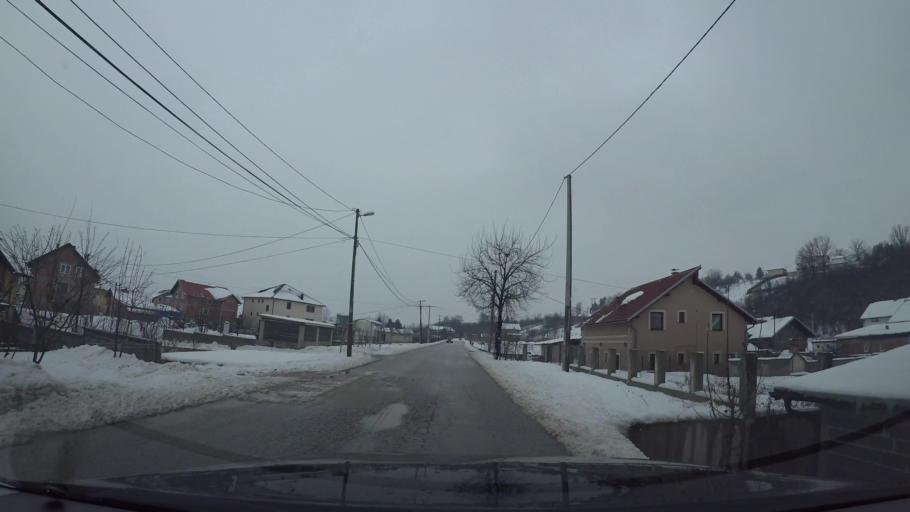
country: BA
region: Federation of Bosnia and Herzegovina
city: Hadzici
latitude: 43.8529
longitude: 18.2754
